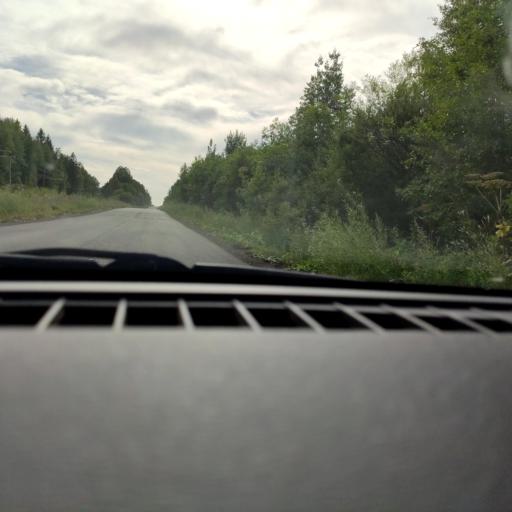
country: RU
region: Perm
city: Polazna
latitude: 58.3370
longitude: 56.1686
